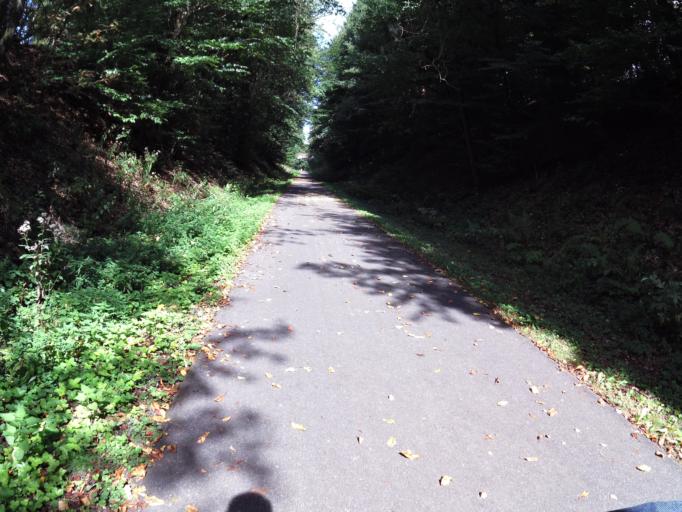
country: DE
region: Rheinland-Pfalz
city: Arzfeld
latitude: 50.0991
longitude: 6.2704
